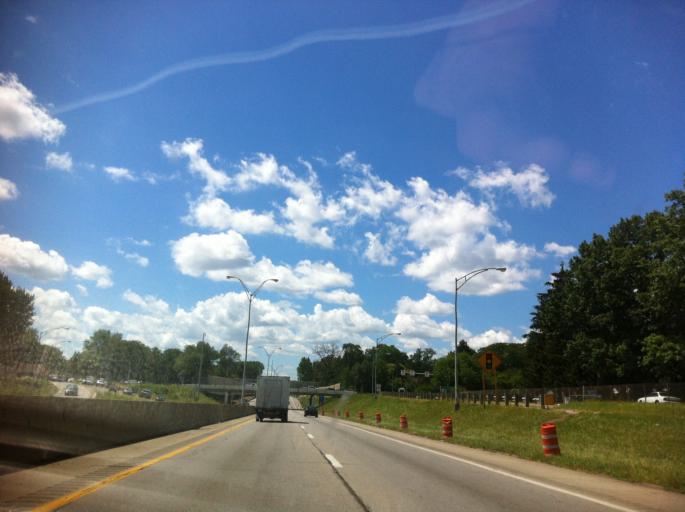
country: US
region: Ohio
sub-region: Lucas County
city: Ottawa Hills
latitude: 41.6881
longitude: -83.6416
